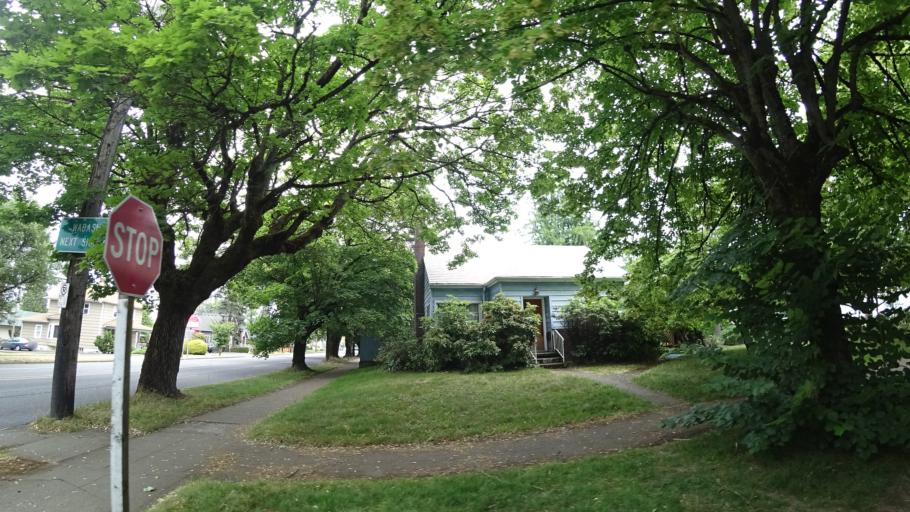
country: US
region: Oregon
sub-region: Multnomah County
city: Portland
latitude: 45.5770
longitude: -122.7048
